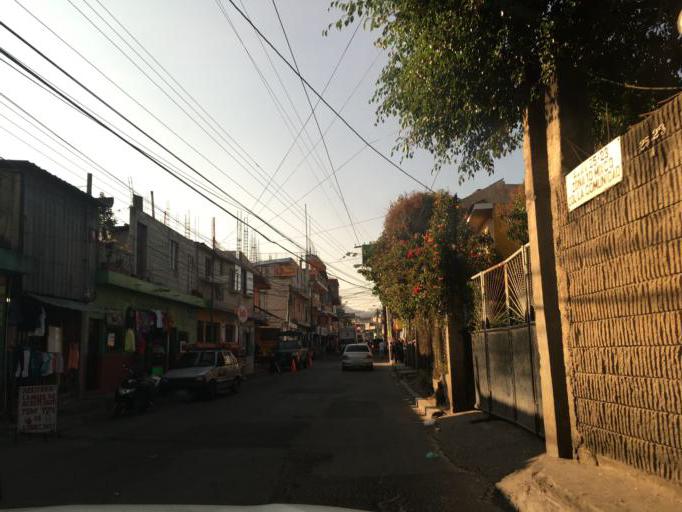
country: GT
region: Guatemala
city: Mixco
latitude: 14.6189
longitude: -90.5818
